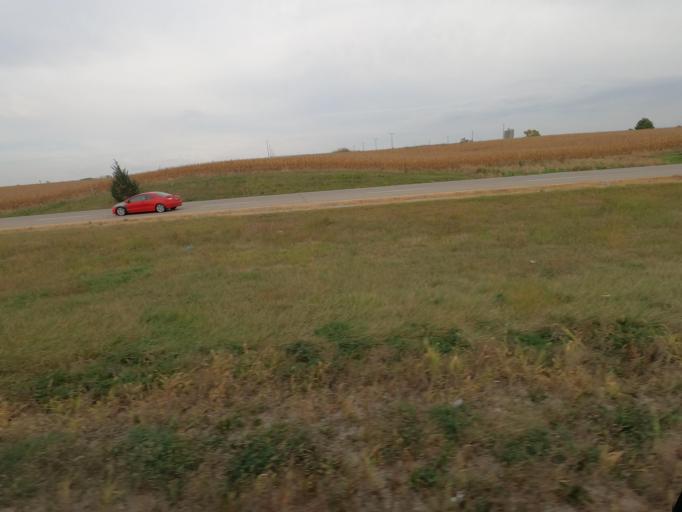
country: US
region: Iowa
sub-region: Marion County
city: Pella
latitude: 41.3896
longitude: -92.9197
